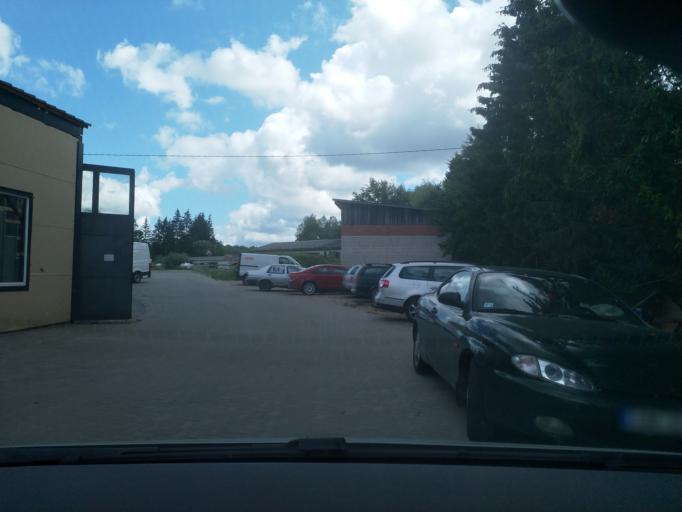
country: LV
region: Kuldigas Rajons
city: Kuldiga
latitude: 56.9799
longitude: 22.0129
